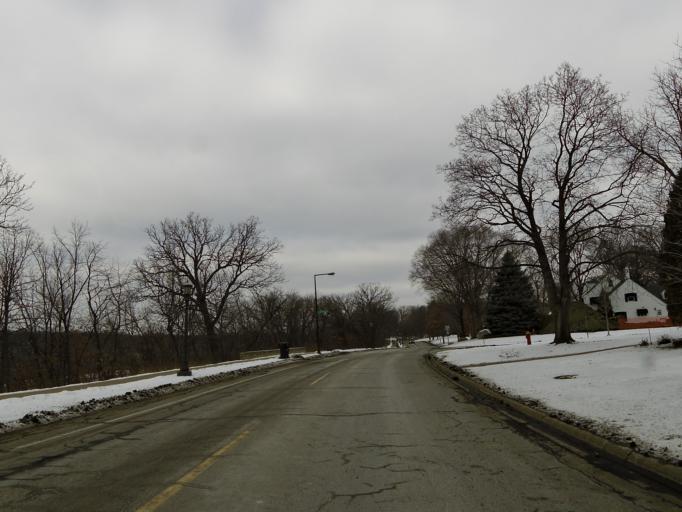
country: US
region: Minnesota
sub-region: Ramsey County
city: Lauderdale
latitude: 44.9302
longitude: -93.1976
